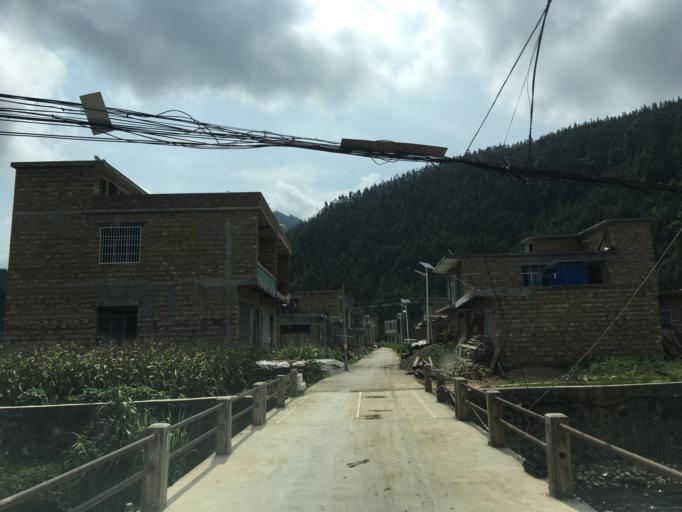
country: CN
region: Guangxi Zhuangzu Zizhiqu
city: Xinzhou
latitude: 24.8843
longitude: 105.8362
